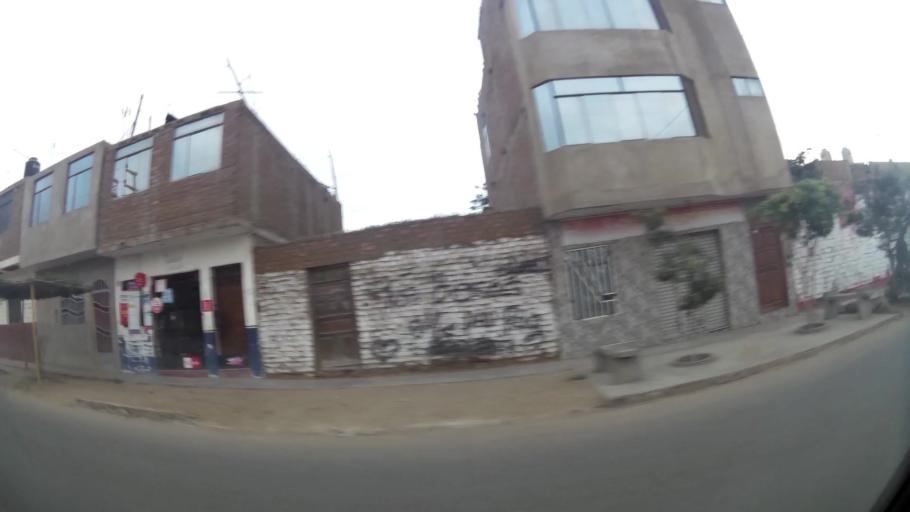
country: PE
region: La Libertad
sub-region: Provincia de Trujillo
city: El Porvenir
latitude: -8.0789
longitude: -79.0198
